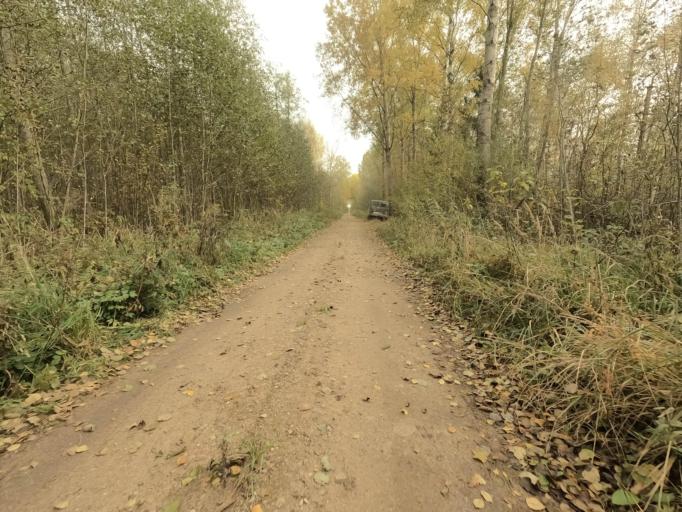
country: RU
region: Novgorod
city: Batetskiy
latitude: 58.8794
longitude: 30.7789
